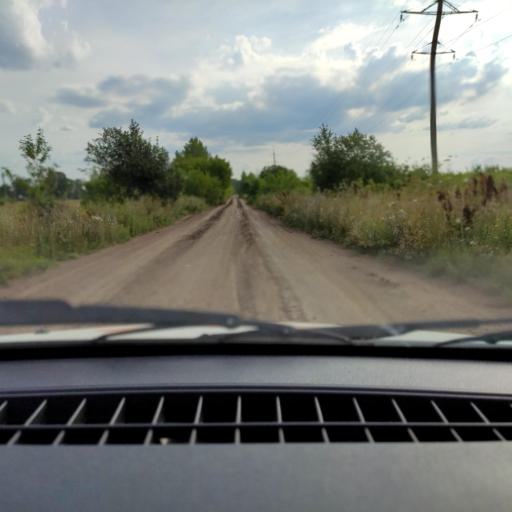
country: RU
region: Bashkortostan
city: Blagoveshchensk
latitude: 54.9239
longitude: 55.9416
